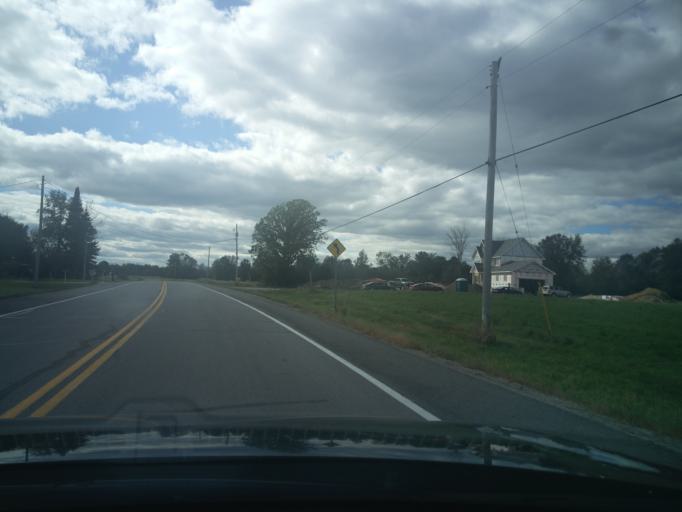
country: CA
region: Ontario
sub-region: Lanark County
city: Smiths Falls
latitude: 44.9787
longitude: -76.1326
